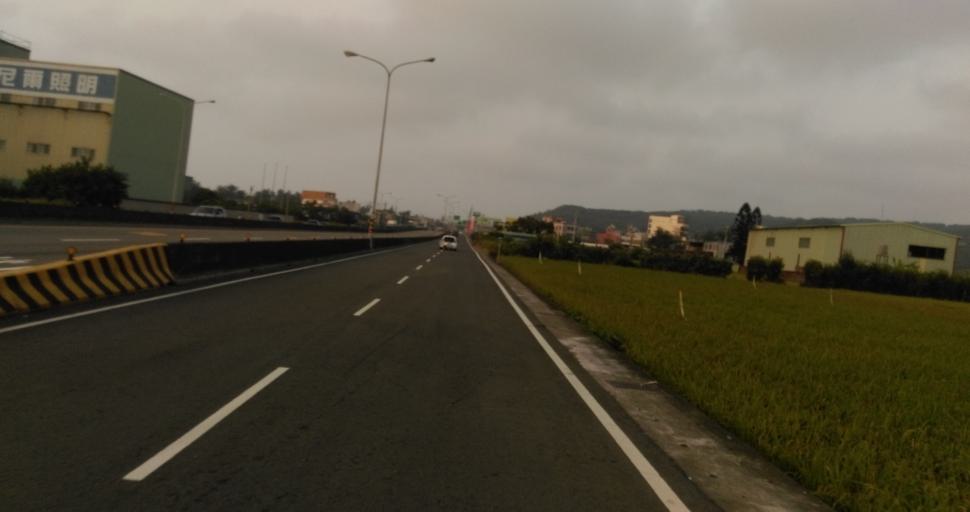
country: TW
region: Taiwan
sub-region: Hsinchu
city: Zhubei
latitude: 24.8684
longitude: 120.9535
